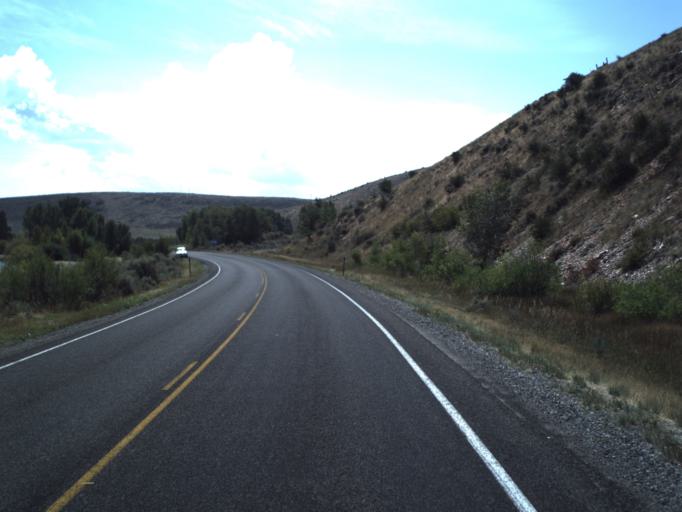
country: US
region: Utah
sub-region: Rich County
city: Randolph
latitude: 41.8610
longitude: -111.3655
